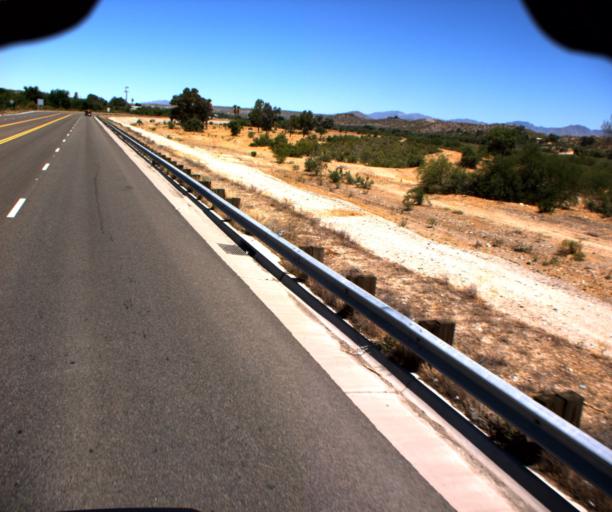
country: US
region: Arizona
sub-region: Maricopa County
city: Wickenburg
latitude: 33.9733
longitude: -112.7301
